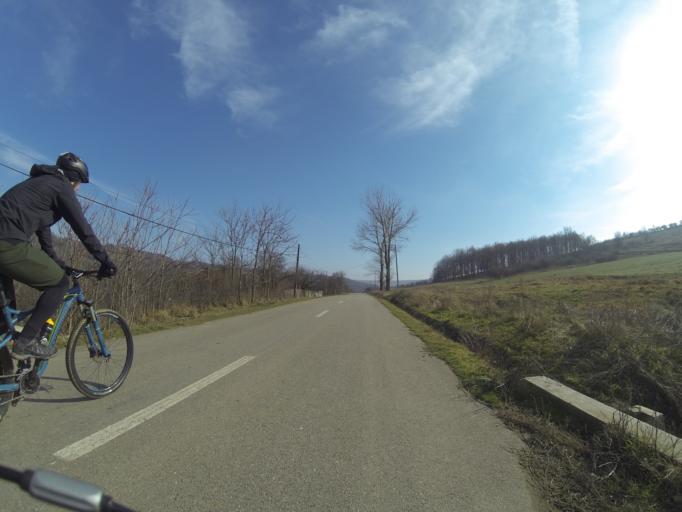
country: RO
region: Mehedinti
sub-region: Comuna Poroina Mare
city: Poroina Mare
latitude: 44.4936
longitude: 22.9301
